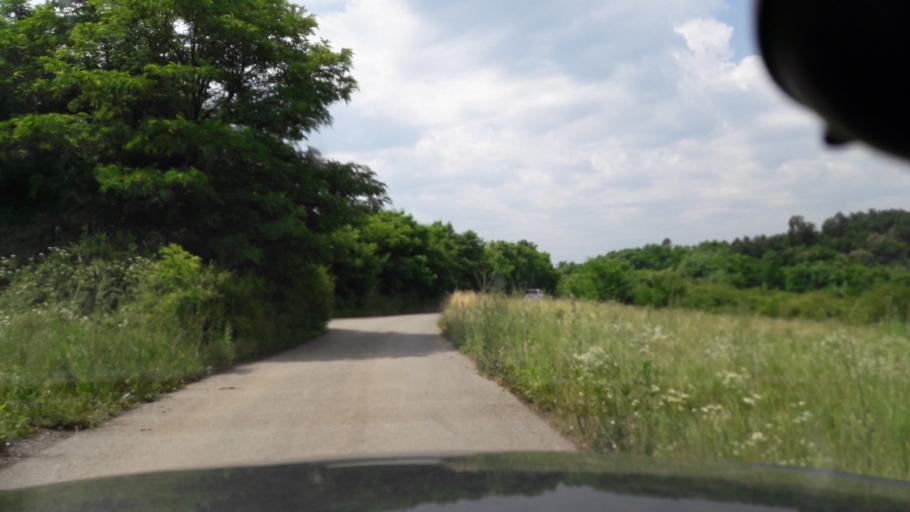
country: RS
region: Central Serbia
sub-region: Belgrade
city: Sopot
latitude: 44.6158
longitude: 20.5996
